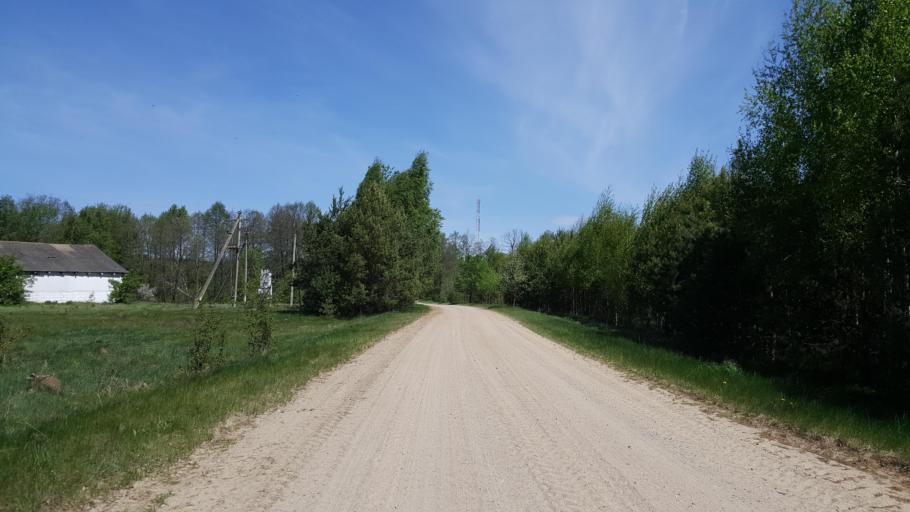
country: BY
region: Brest
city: Zhabinka
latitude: 52.3607
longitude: 24.0588
